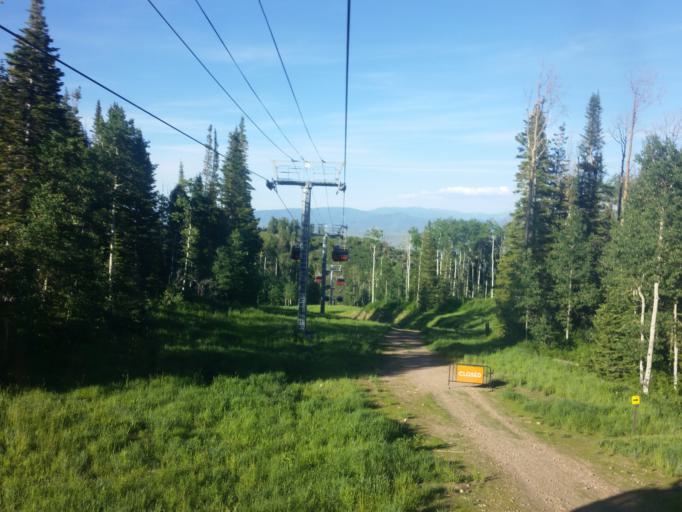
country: US
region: Utah
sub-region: Summit County
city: Snyderville
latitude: 40.6786
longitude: -111.5768
